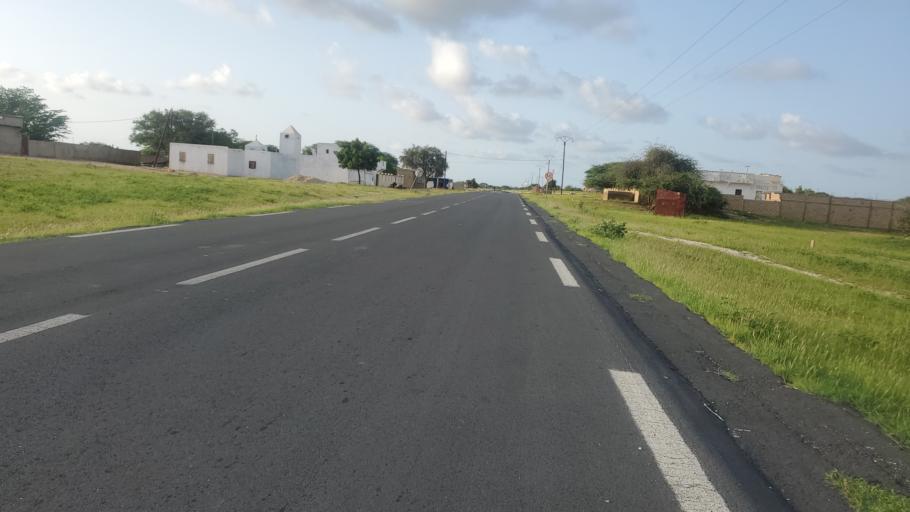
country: SN
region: Saint-Louis
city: Saint-Louis
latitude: 16.1522
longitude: -16.4098
